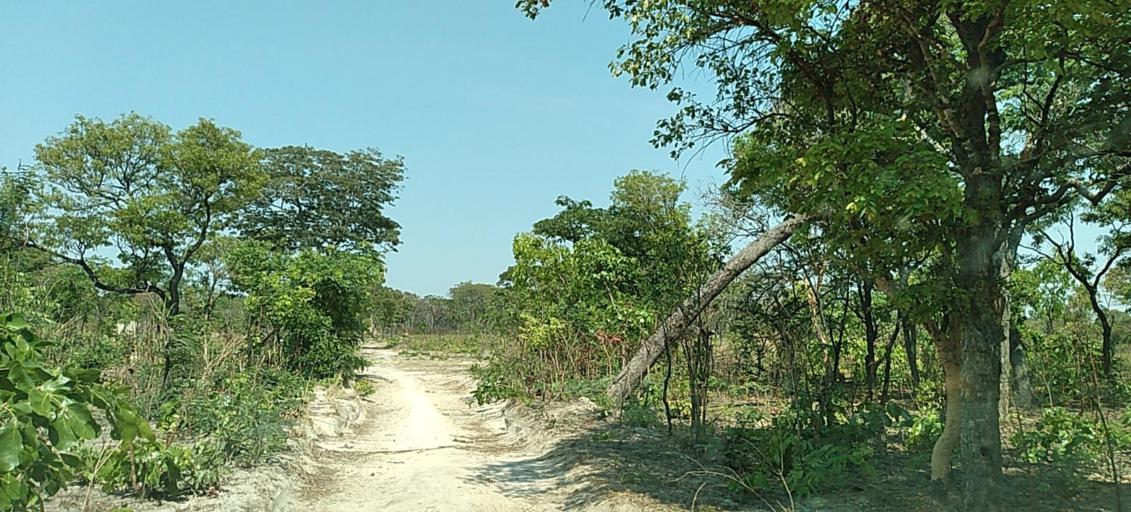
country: ZM
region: Copperbelt
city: Mpongwe
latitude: -13.7767
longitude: 28.1079
